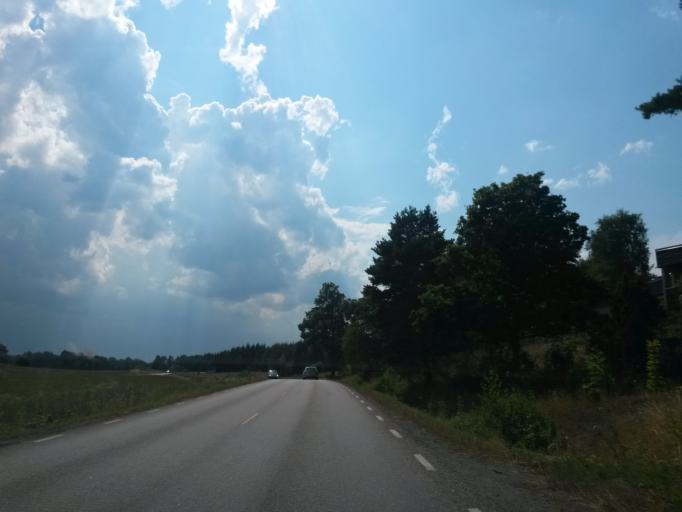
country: SE
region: Vaestra Goetaland
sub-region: Lidkopings Kommun
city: Lidkoping
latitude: 58.6427
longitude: 13.1472
